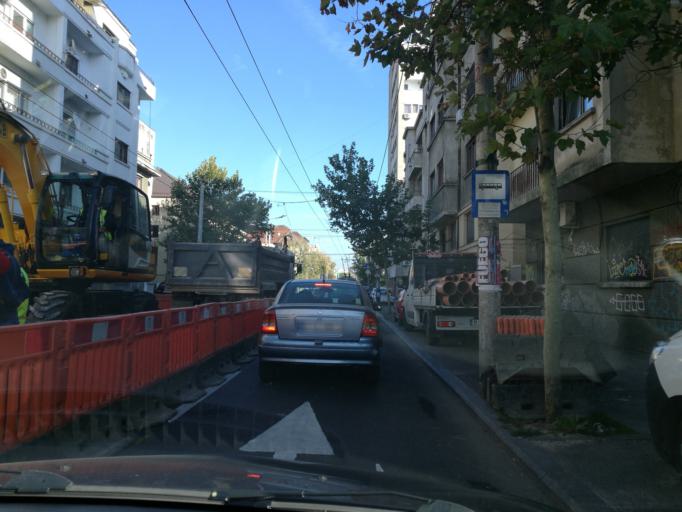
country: RO
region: Bucuresti
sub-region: Municipiul Bucuresti
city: Bucharest
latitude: 44.4460
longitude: 26.1084
